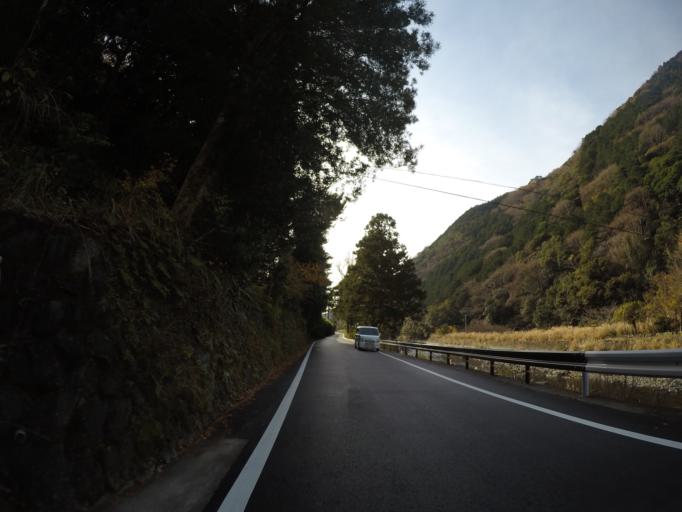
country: JP
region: Shizuoka
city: Heda
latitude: 34.7969
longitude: 138.8076
